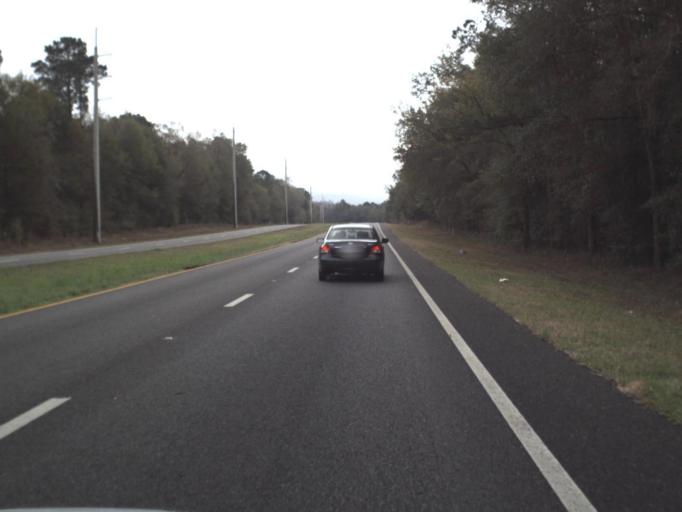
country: US
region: Florida
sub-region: Leon County
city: Woodville
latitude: 30.4172
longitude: -84.0892
